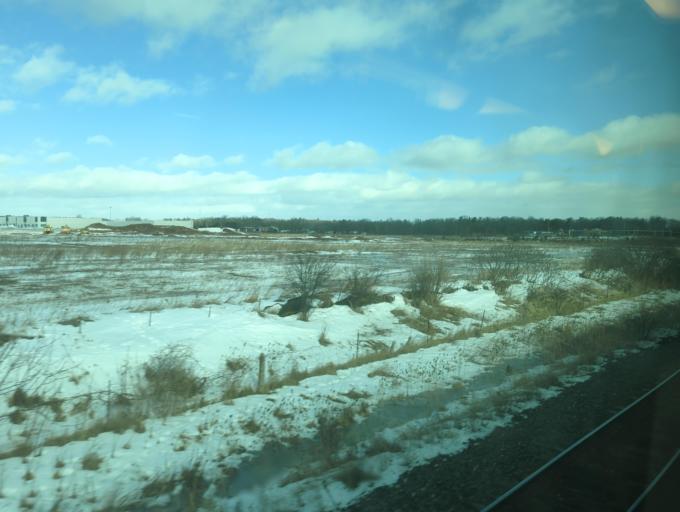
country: CA
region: Ontario
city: Oakville
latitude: 43.3968
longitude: -79.7440
